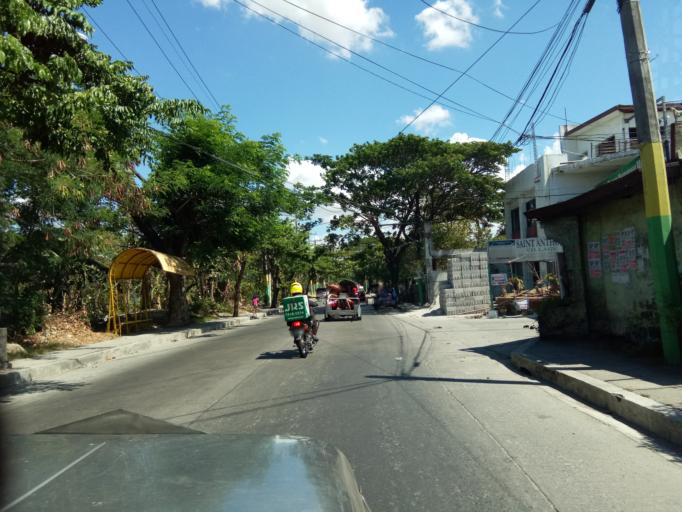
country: PH
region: Calabarzon
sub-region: Province of Cavite
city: Dasmarinas
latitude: 14.3478
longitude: 120.9454
